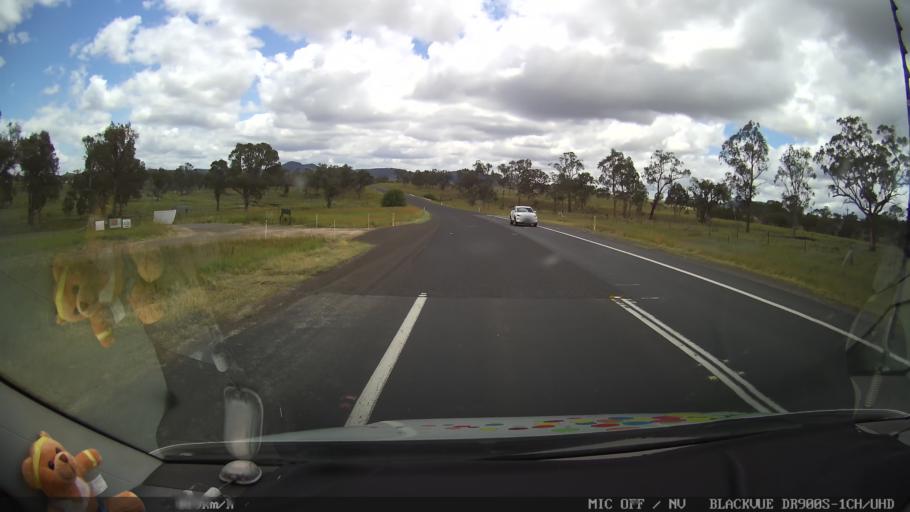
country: AU
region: New South Wales
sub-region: Glen Innes Severn
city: Glen Innes
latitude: -29.3885
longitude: 151.8879
